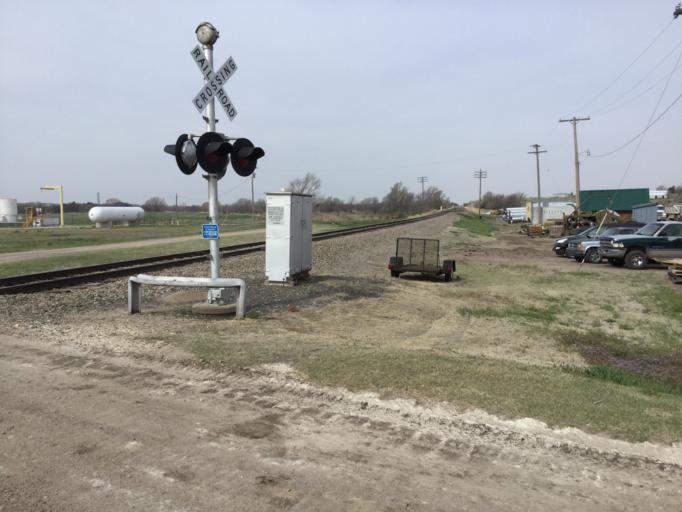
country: US
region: Kansas
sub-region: Norton County
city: Norton
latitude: 39.8270
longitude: -99.9001
